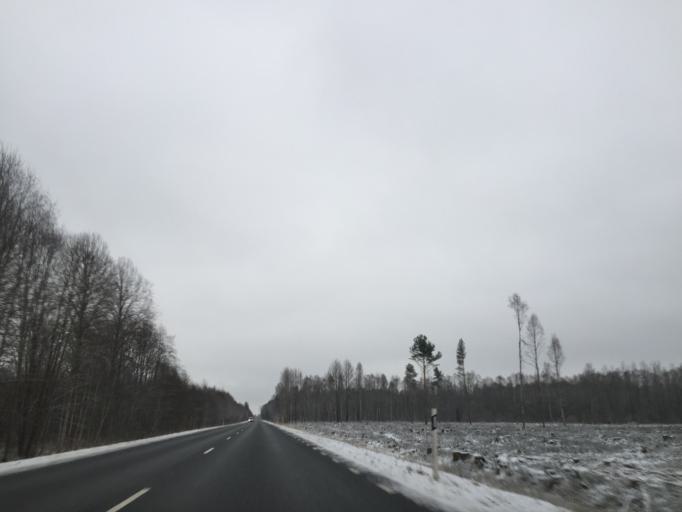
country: EE
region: Laeaene
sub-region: Lihula vald
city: Lihula
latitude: 58.6481
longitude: 23.8437
